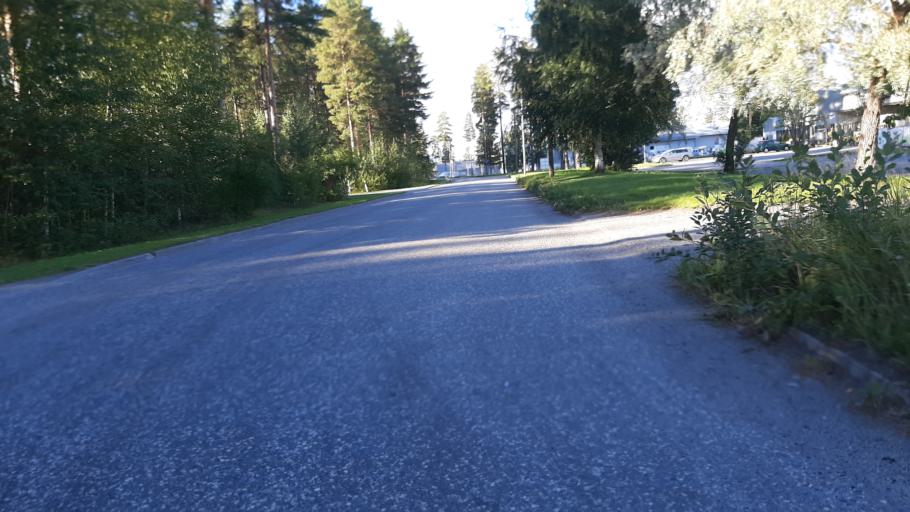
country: FI
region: North Karelia
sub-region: Joensuu
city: Joensuu
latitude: 62.6246
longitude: 29.7708
